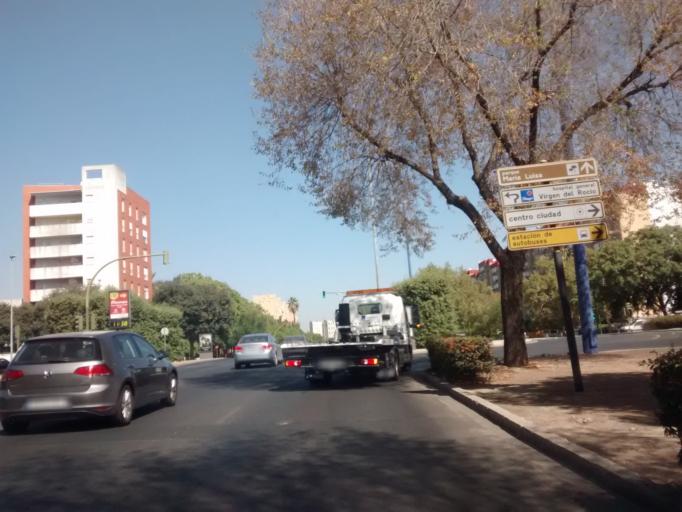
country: ES
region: Andalusia
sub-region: Provincia de Sevilla
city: Sevilla
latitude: 37.3692
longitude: -5.9688
